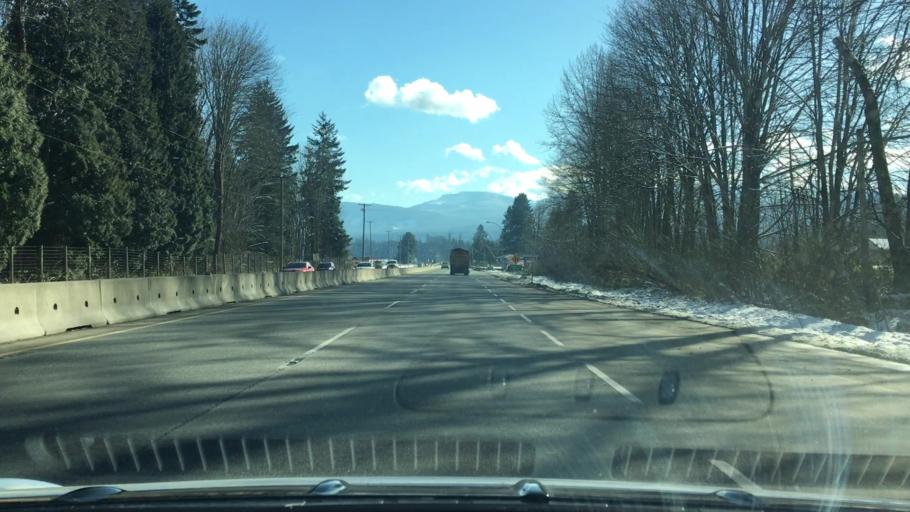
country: CA
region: British Columbia
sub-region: Cowichan Valley Regional District
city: Ladysmith
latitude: 49.0591
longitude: -123.8777
